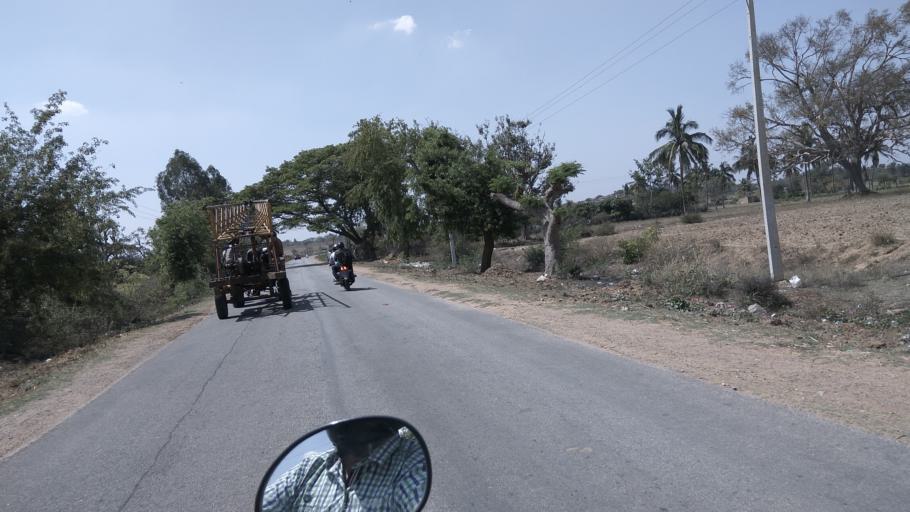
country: IN
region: Karnataka
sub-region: Kolar
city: Mulbagal
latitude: 13.1675
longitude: 78.3637
